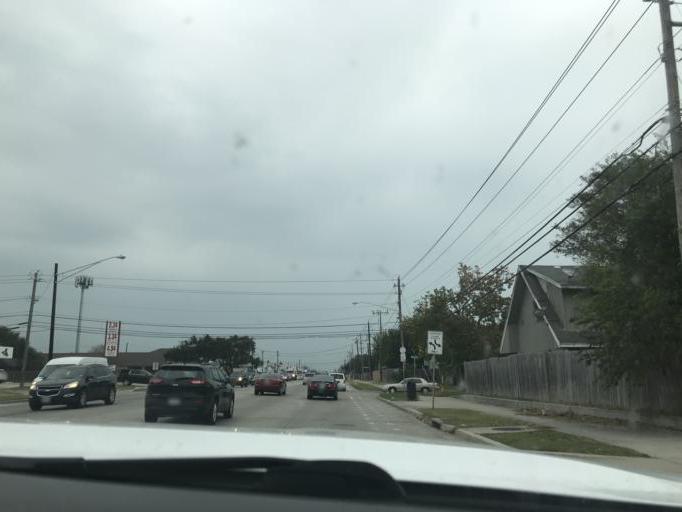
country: US
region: Texas
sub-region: Nueces County
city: Corpus Christi
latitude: 27.6993
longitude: -97.3751
